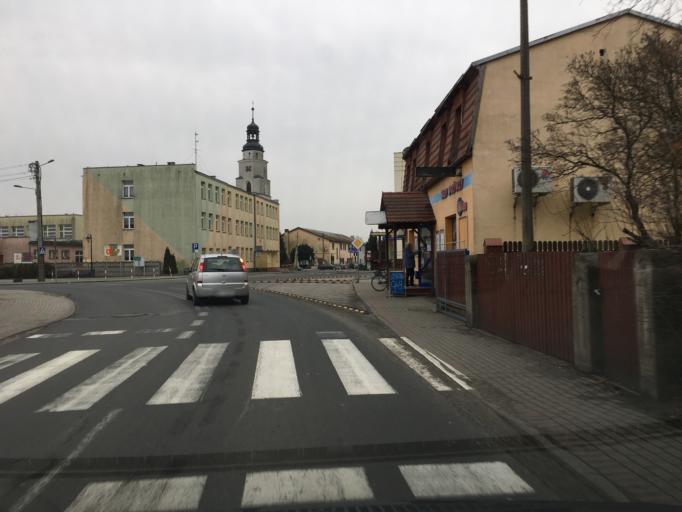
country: PL
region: Opole Voivodeship
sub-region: Powiat kedzierzynsko-kozielski
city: Bierawa
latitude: 50.2805
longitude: 18.2416
